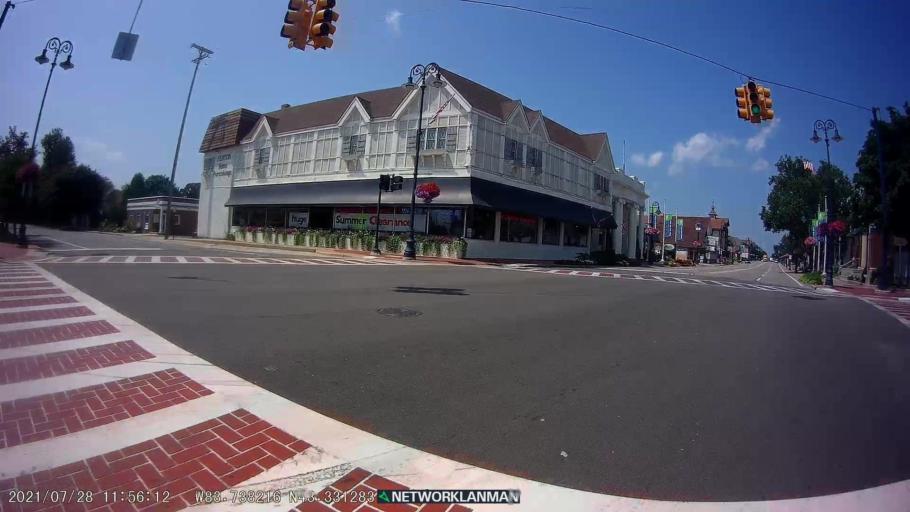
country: US
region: Michigan
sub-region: Saginaw County
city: Frankenmuth
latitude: 43.3318
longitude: -83.7358
